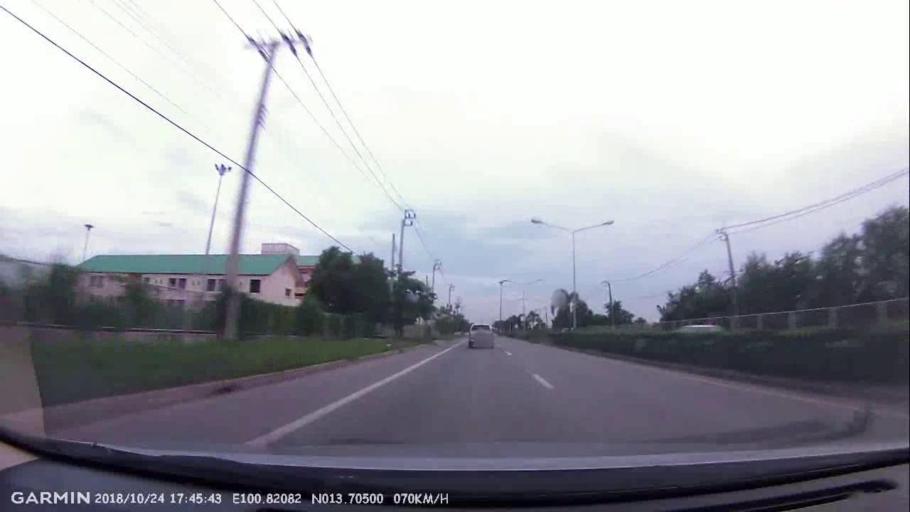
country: TH
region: Bangkok
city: Lat Krabang
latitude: 13.7048
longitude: 100.8209
